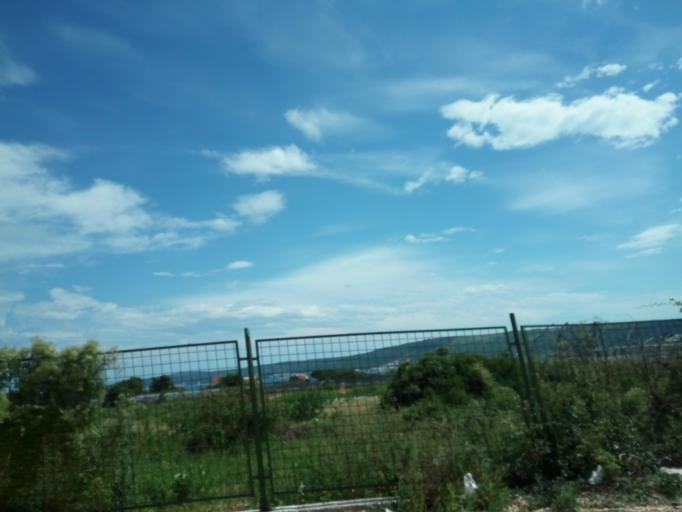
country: HR
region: Splitsko-Dalmatinska
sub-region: Grad Trogir
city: Trogir
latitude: 43.5374
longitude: 16.3040
